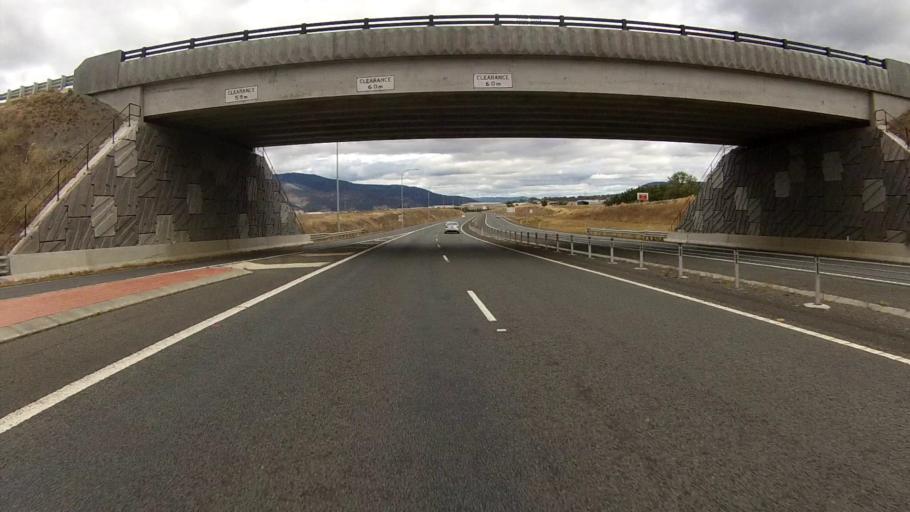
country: AU
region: Tasmania
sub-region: Brighton
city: Bridgewater
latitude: -42.7138
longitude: 147.2455
